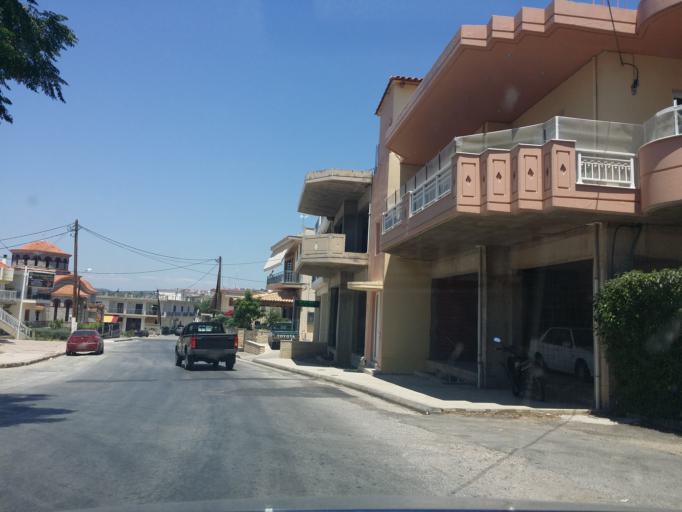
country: GR
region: Peloponnese
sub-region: Nomos Lakonias
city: Vlakhiotis
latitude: 36.8622
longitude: 22.7124
